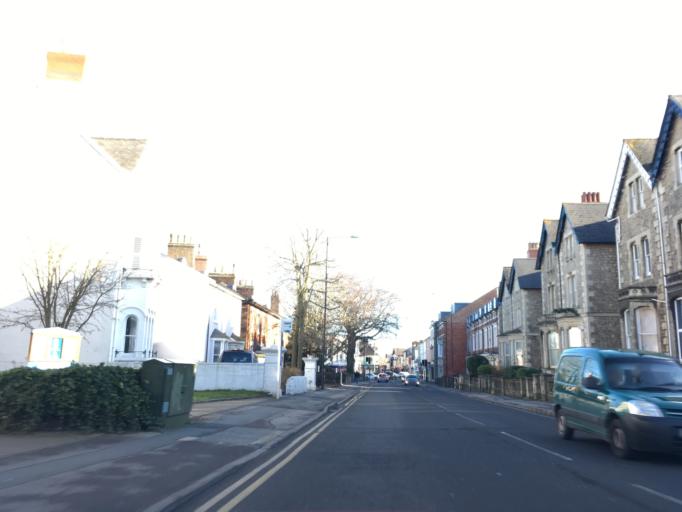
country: GB
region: England
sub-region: Borough of Swindon
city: Swindon
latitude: 51.5526
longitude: -1.7795
